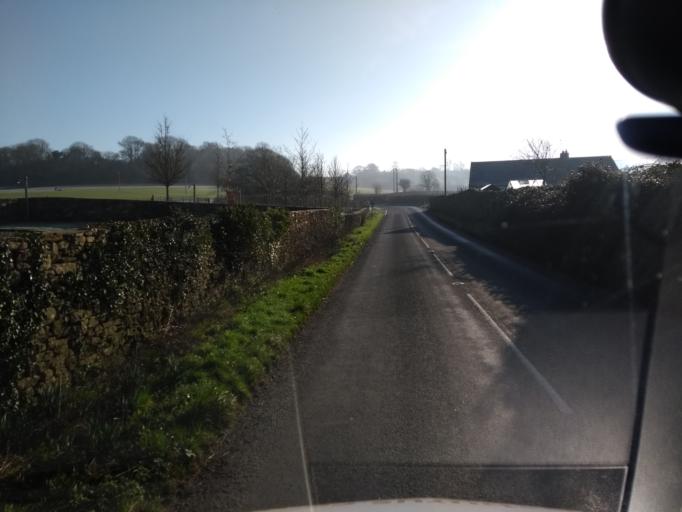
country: GB
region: England
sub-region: Somerset
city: Bruton
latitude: 51.1083
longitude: -2.4474
